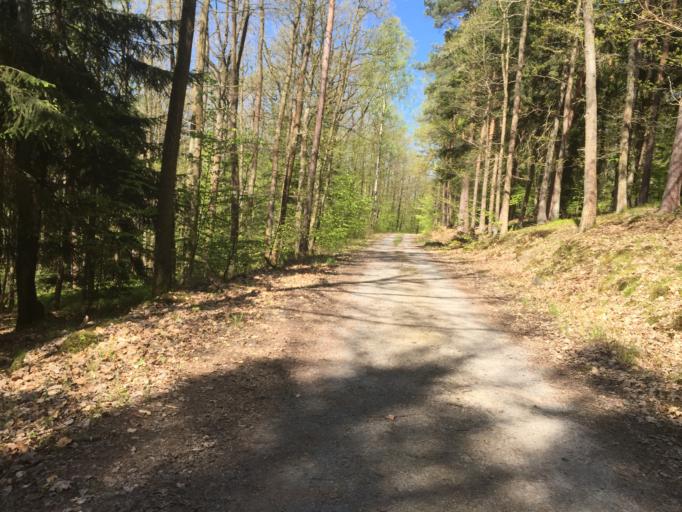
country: DE
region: Bavaria
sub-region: Regierungsbezirk Unterfranken
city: Sulzfeld
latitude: 50.2590
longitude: 10.4245
